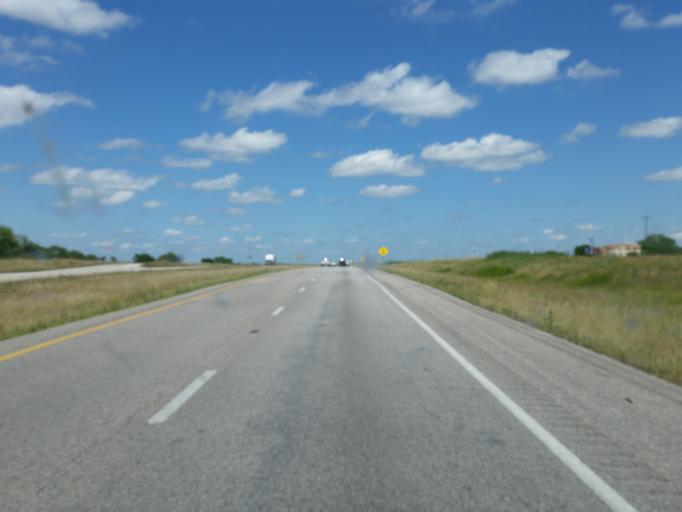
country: US
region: Texas
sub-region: Eastland County
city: Cisco
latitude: 32.3747
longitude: -99.1763
